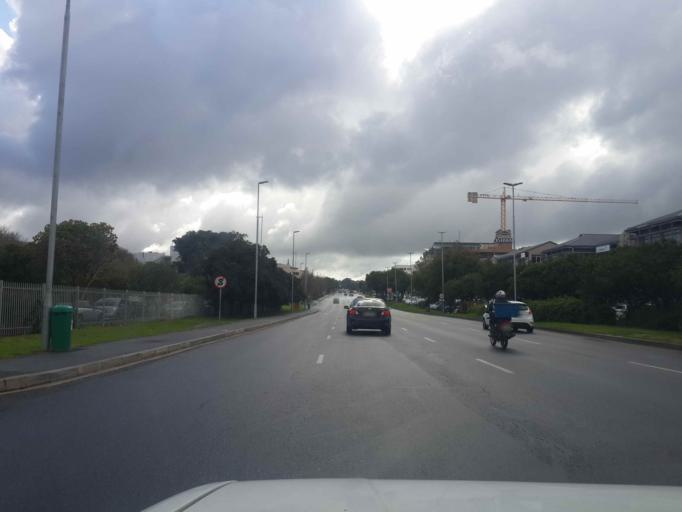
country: ZA
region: Western Cape
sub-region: City of Cape Town
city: Kraaifontein
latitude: -33.8842
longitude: 18.6346
